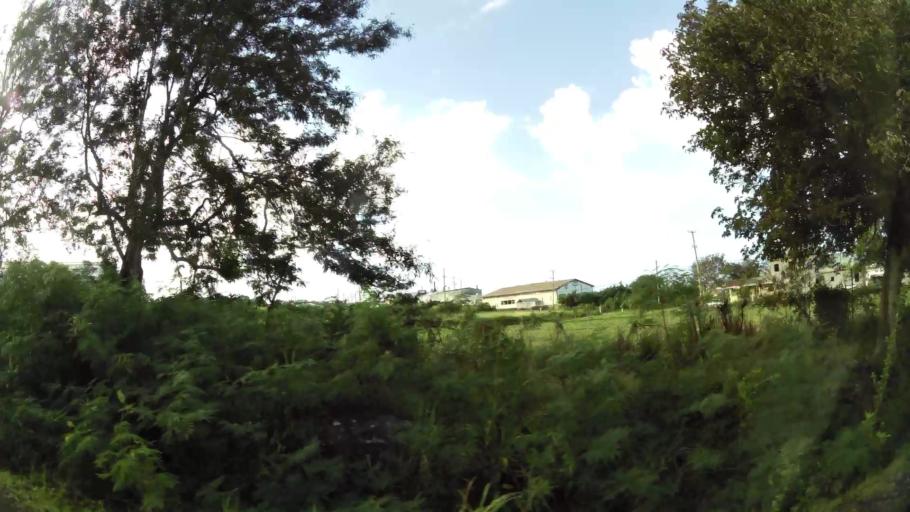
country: KN
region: Saint Paul Charlestown
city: Charlestown
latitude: 17.1280
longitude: -62.6096
